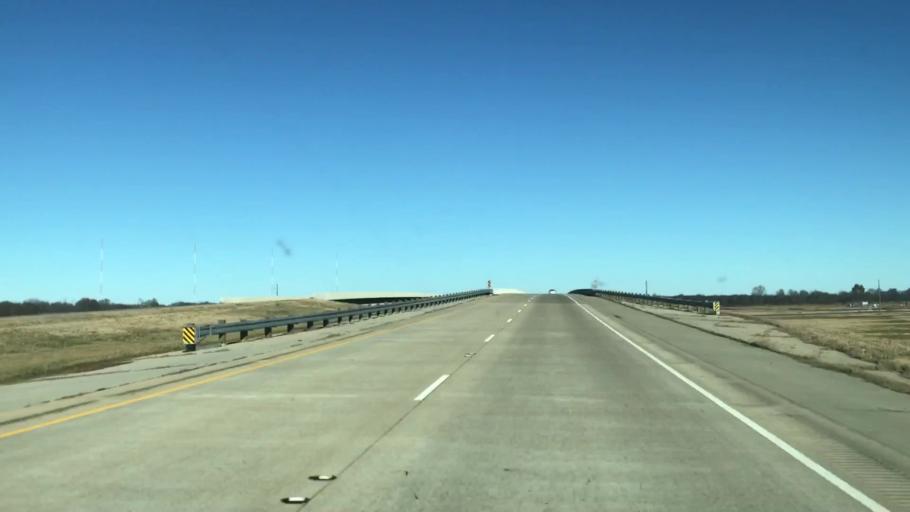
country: US
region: Louisiana
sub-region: Caddo Parish
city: Blanchard
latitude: 32.6731
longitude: -93.8494
